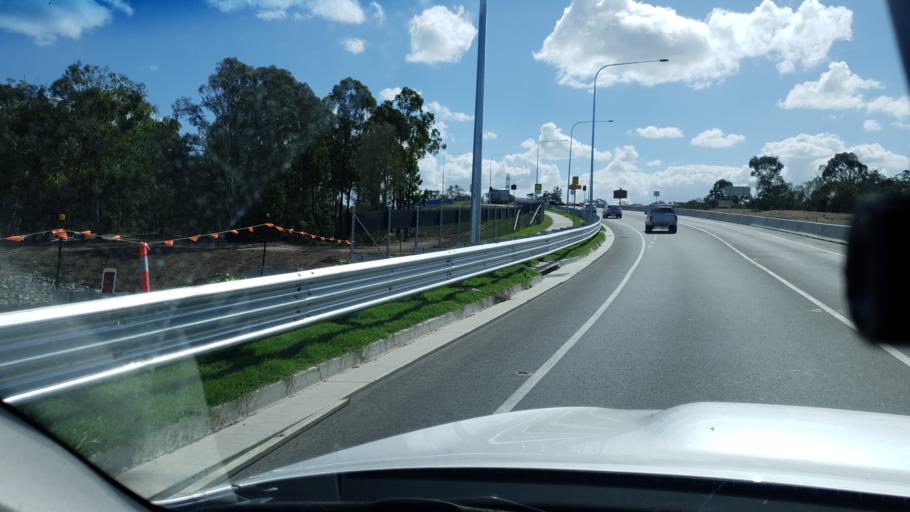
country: AU
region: Queensland
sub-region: Logan
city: Woodridge
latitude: -27.6512
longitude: 153.0725
